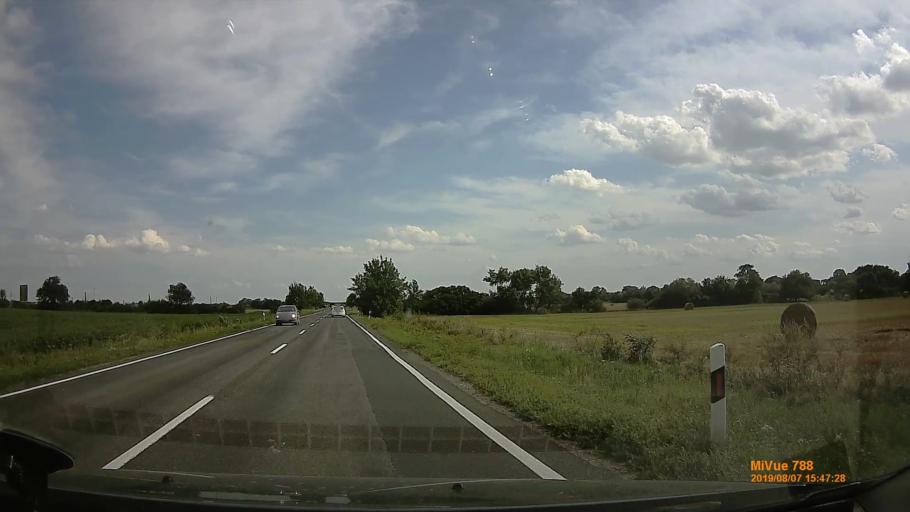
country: HU
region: Vas
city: Jak
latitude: 47.1710
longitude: 16.6277
